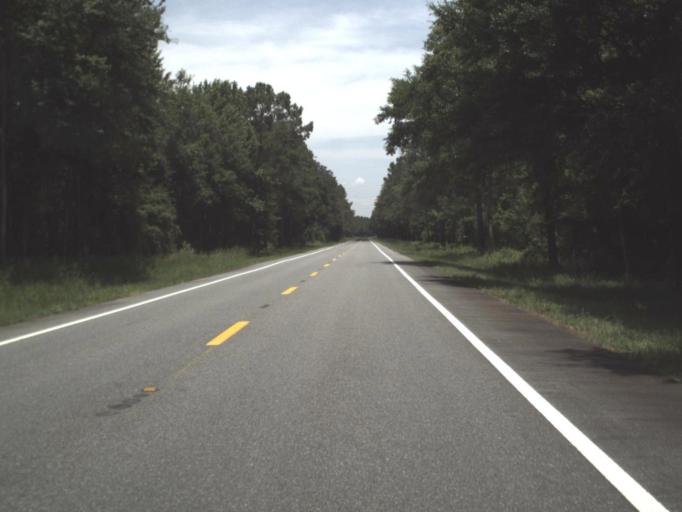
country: US
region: Florida
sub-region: Lafayette County
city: Mayo
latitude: 29.9069
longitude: -83.2928
